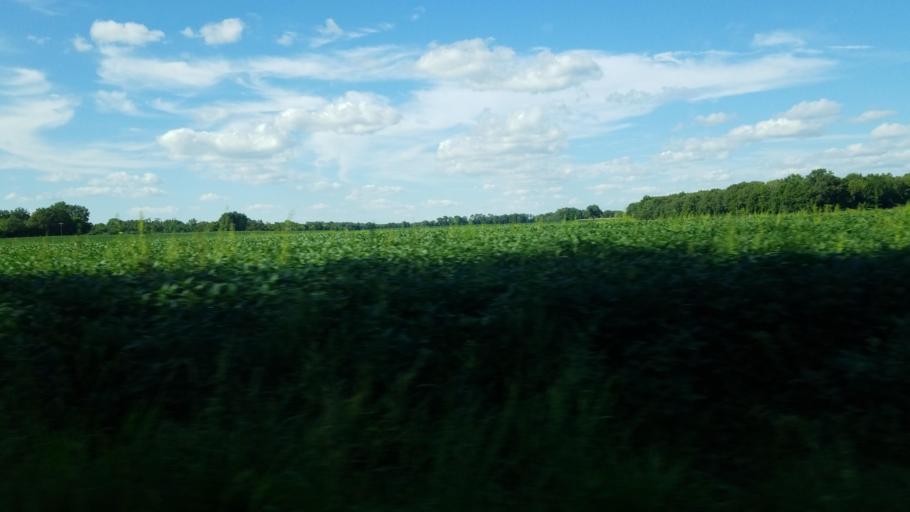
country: US
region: Illinois
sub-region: Saline County
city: Harrisburg
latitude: 37.8127
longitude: -88.5648
